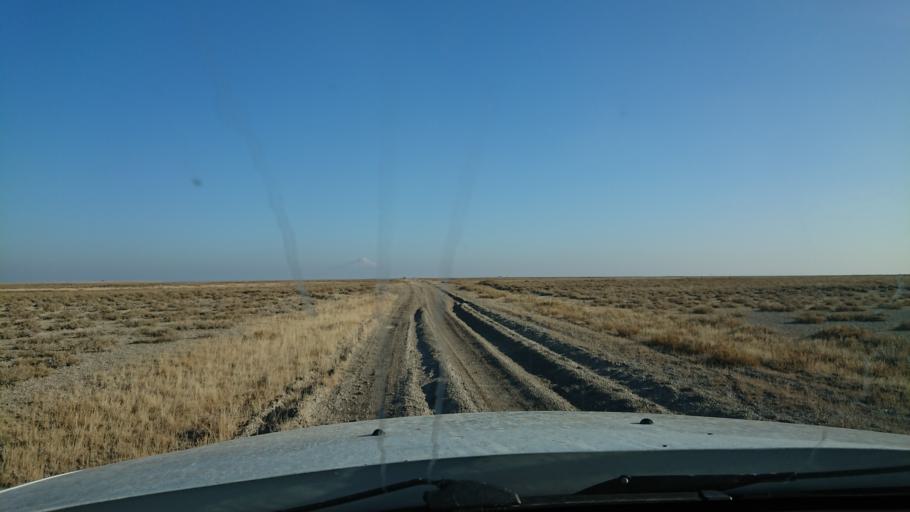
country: TR
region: Aksaray
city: Sultanhani
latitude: 38.4047
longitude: 33.5739
